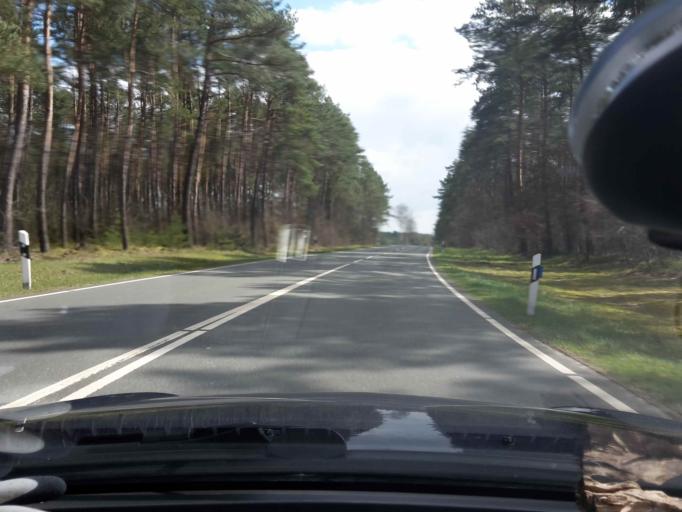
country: DE
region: Lower Saxony
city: Bispingen
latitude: 53.0903
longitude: 10.0455
